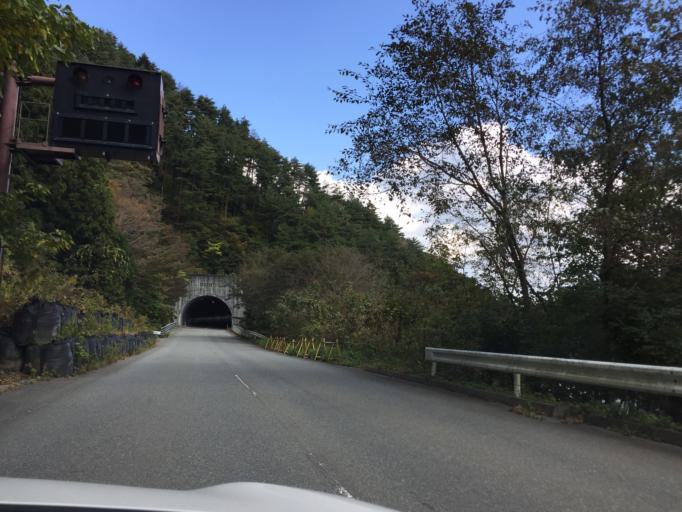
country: JP
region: Fukushima
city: Namie
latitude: 37.3581
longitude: 140.9209
